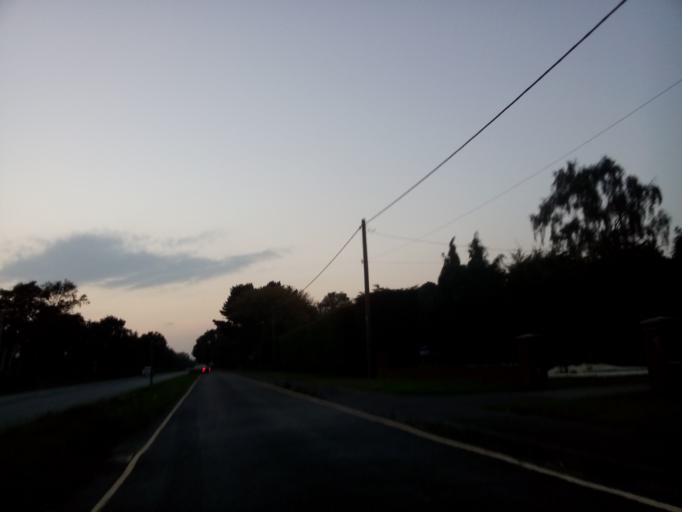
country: GB
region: England
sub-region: Suffolk
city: Kesgrave
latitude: 52.0292
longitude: 1.2257
